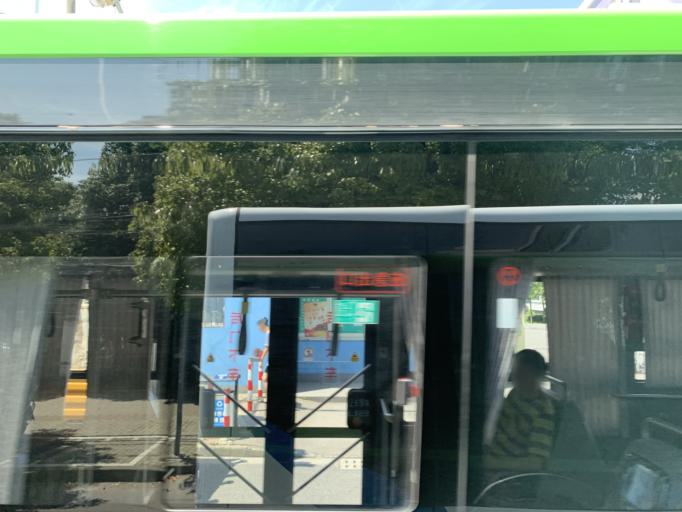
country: CN
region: Shanghai Shi
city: Huamu
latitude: 31.1732
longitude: 121.5363
